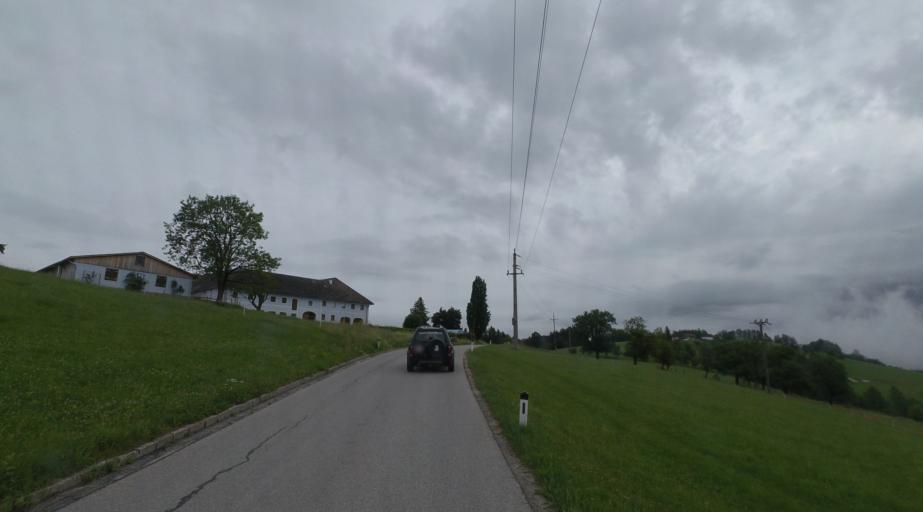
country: AT
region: Upper Austria
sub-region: Politischer Bezirk Kirchdorf an der Krems
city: Micheldorf in Oberoesterreich
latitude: 47.9241
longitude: 14.1633
